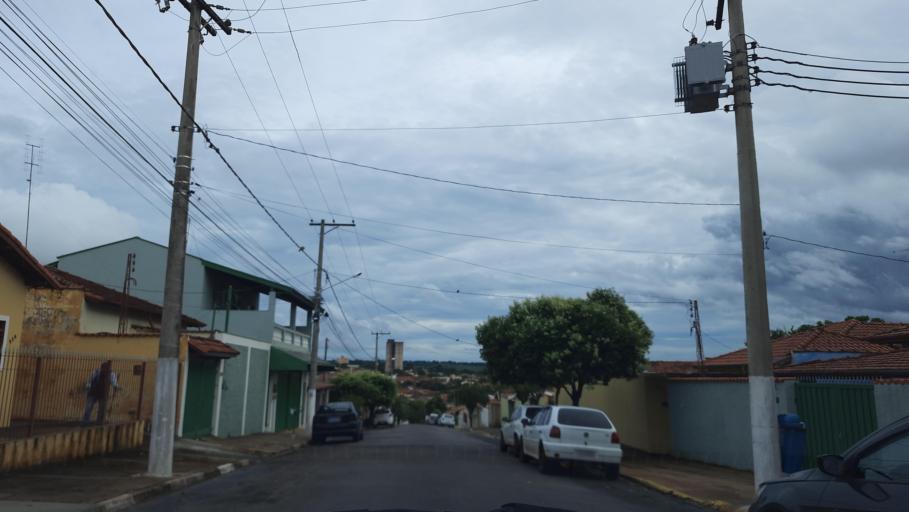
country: BR
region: Sao Paulo
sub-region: Casa Branca
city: Casa Branca
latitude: -21.7654
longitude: -47.0921
